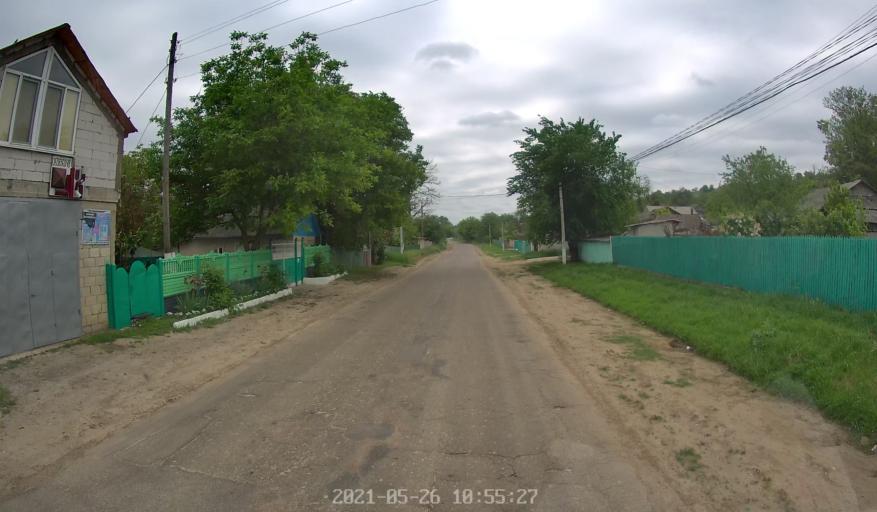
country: MD
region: Hincesti
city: Dancu
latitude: 46.8477
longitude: 28.3842
